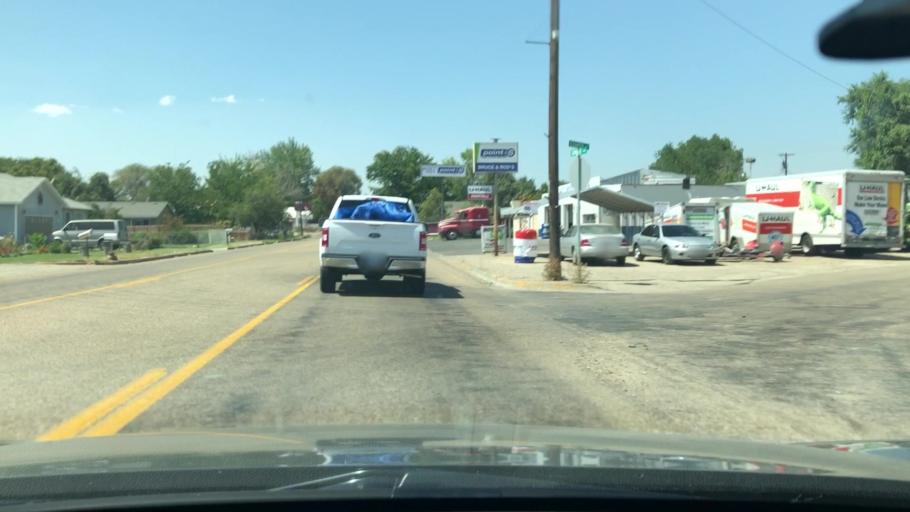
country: US
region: Idaho
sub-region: Canyon County
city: Parma
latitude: 43.7819
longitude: -116.9372
